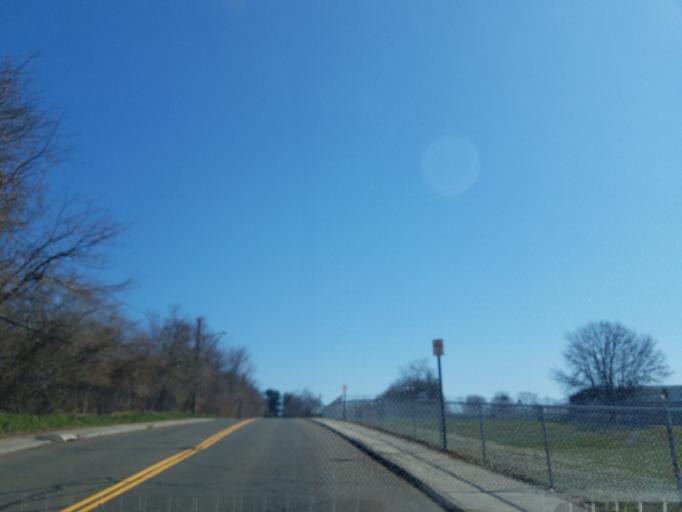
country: US
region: Connecticut
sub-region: Fairfield County
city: Norwalk
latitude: 41.1347
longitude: -73.4173
